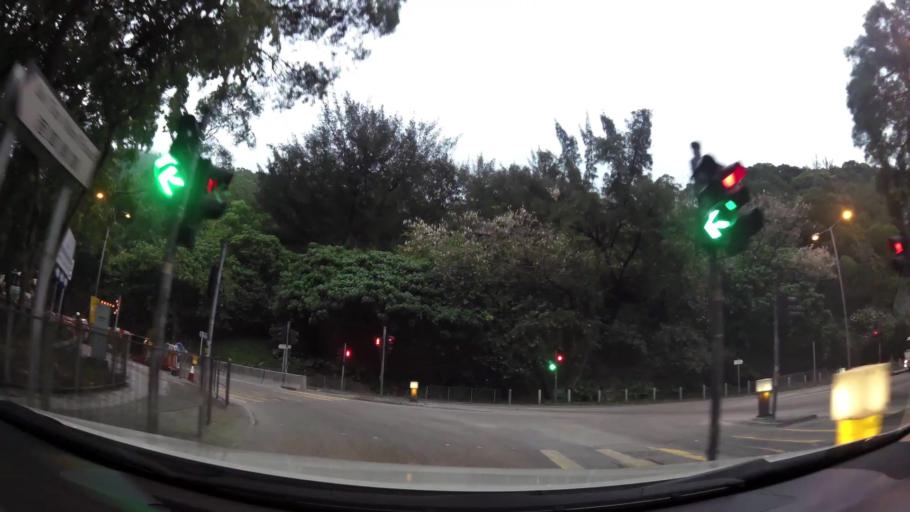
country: HK
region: Tsuen Wan
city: Tsuen Wan
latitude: 22.3389
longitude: 114.0950
